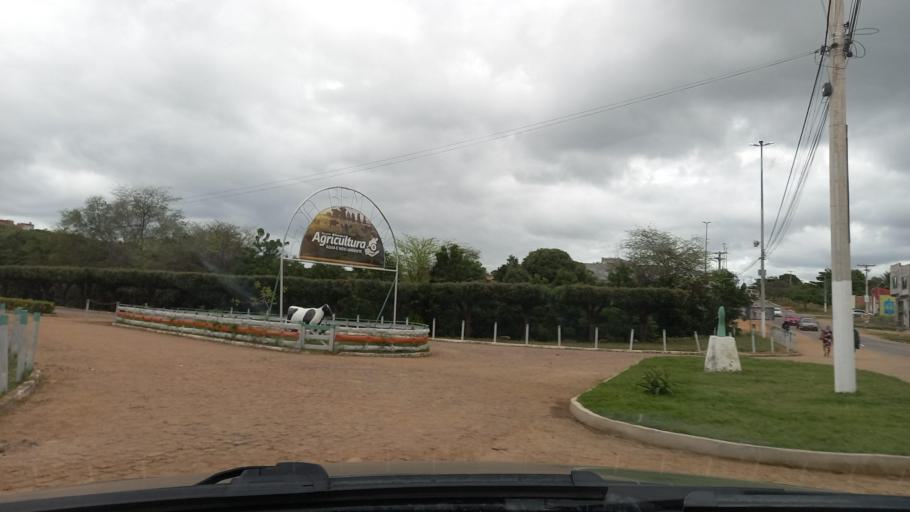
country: BR
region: Sergipe
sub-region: Caninde De Sao Francisco
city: Caninde de Sao Francisco
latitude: -9.6702
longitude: -37.7934
